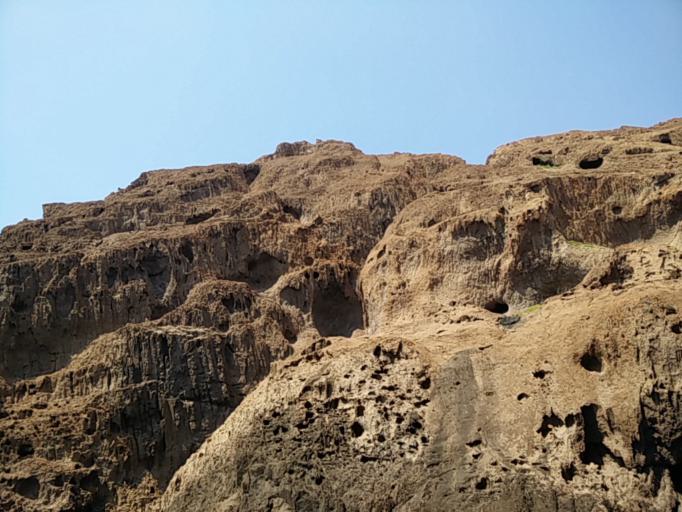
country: FR
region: Corsica
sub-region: Departement de la Corse-du-Sud
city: Cargese
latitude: 42.3462
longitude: 8.5523
